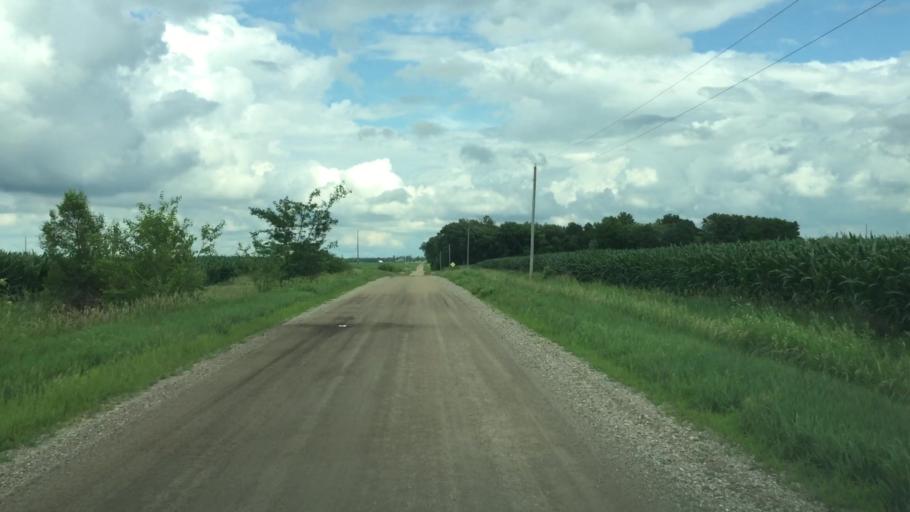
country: US
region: Iowa
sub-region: Jasper County
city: Newton
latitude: 41.7459
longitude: -93.0253
